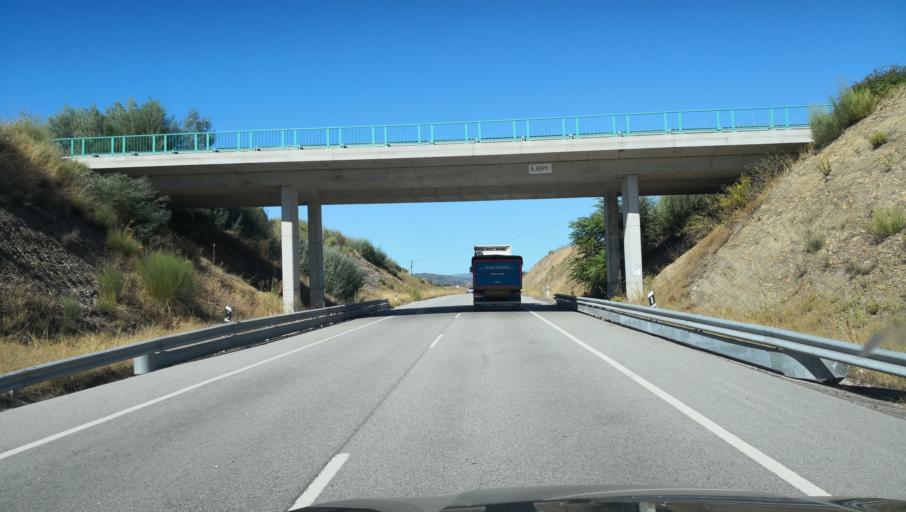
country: PT
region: Braganca
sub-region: Mirandela
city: Mirandela
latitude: 41.5285
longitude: -7.2430
